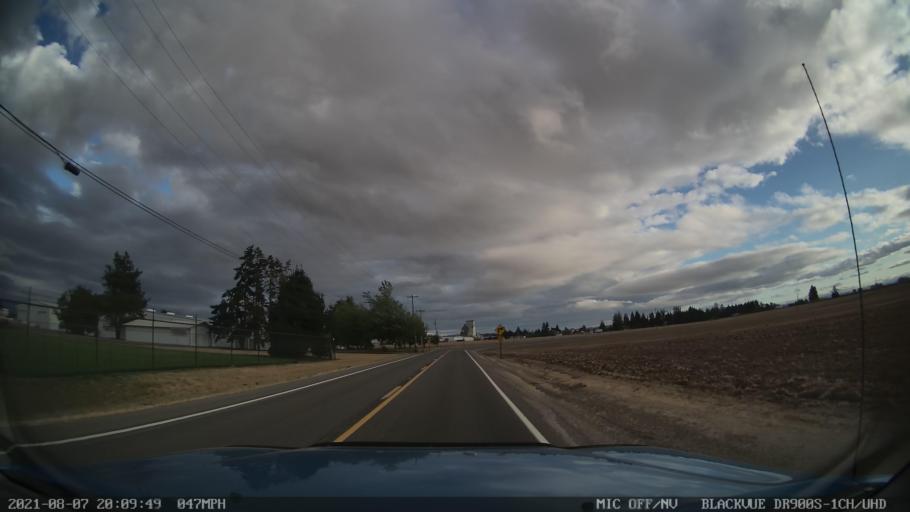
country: US
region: Oregon
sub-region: Marion County
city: Silverton
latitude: 44.9665
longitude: -122.8775
